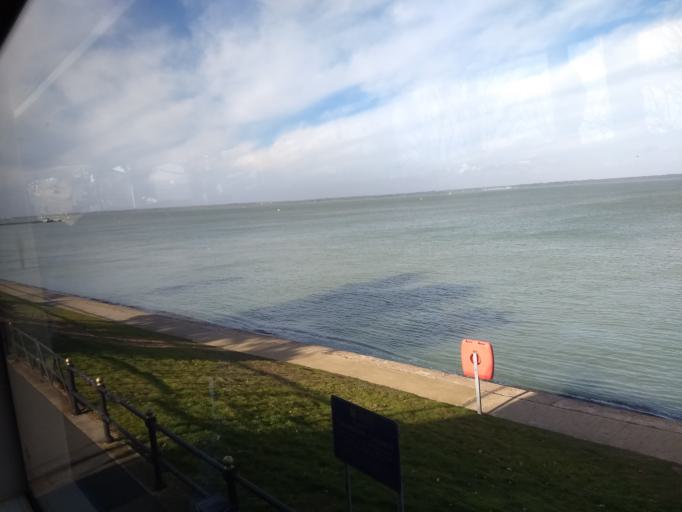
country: GB
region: England
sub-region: Isle of Wight
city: Yarmouth
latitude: 50.7065
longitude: -1.4890
